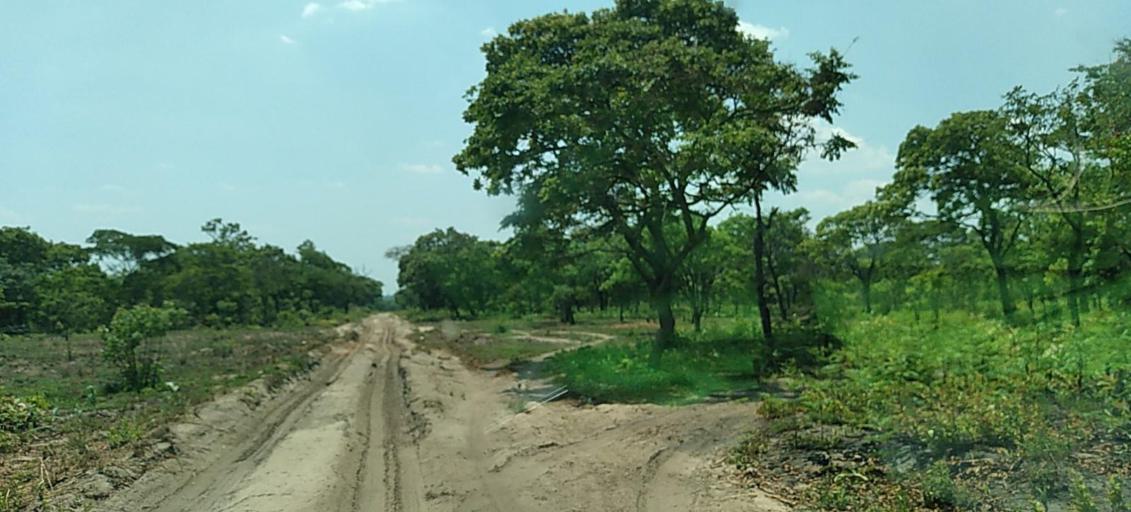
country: CD
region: Katanga
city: Kolwezi
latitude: -11.3030
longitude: 25.2312
